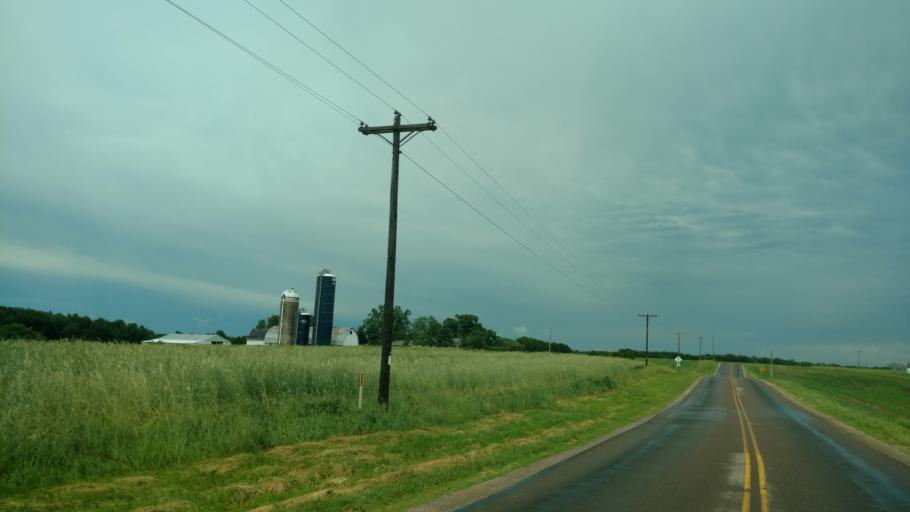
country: US
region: Wisconsin
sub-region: Vernon County
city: Hillsboro
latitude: 43.5970
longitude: -90.4139
